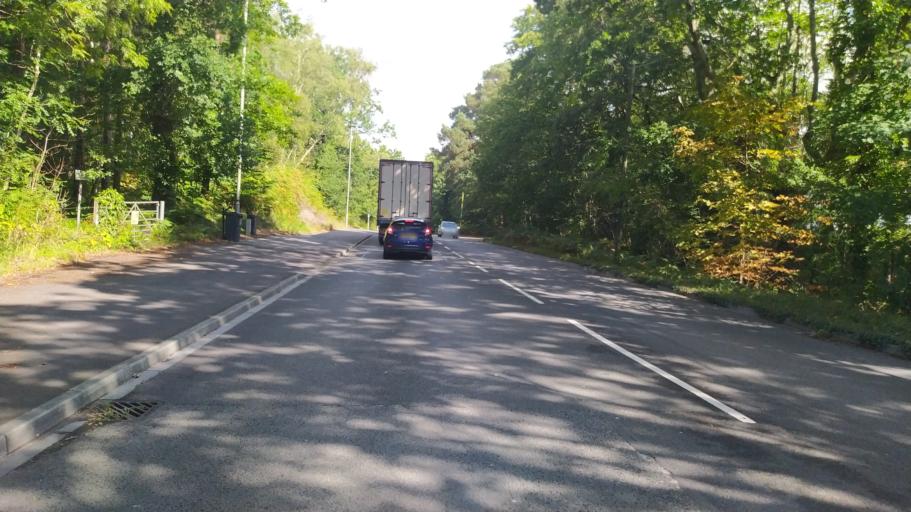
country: GB
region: England
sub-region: Dorset
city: Wimborne Minster
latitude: 50.7678
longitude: -1.9787
